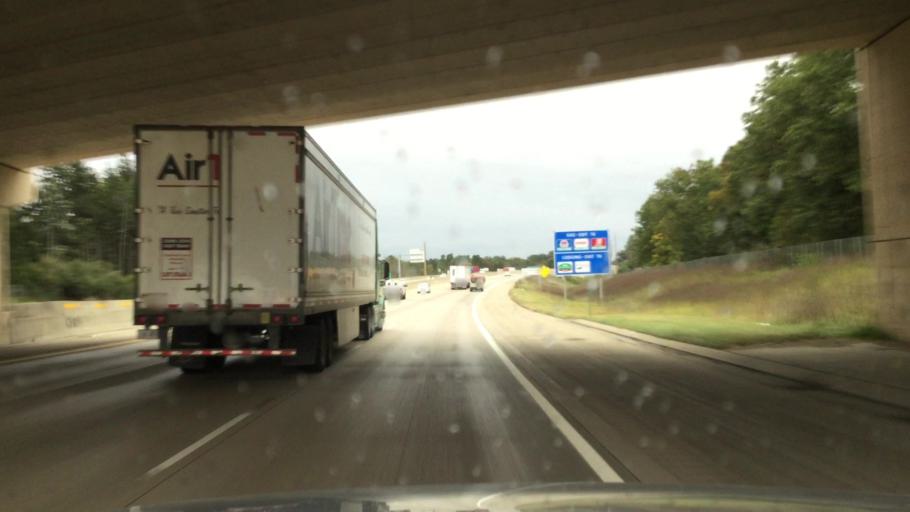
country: US
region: Michigan
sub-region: Kalamazoo County
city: Portage
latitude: 42.2388
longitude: -85.5750
